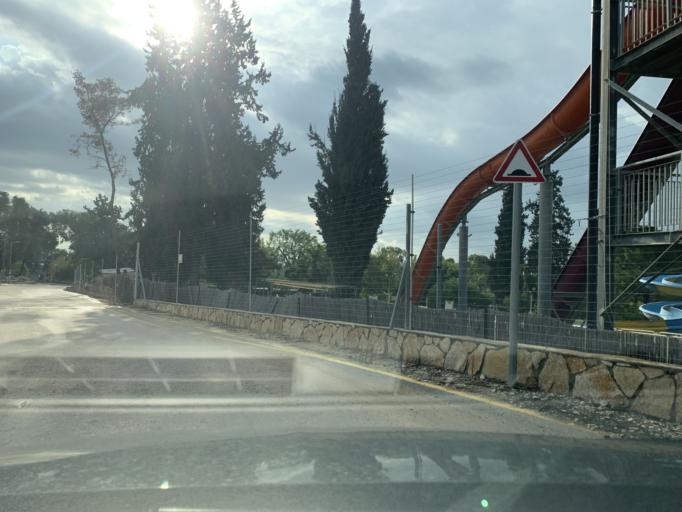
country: IL
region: Central District
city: Rosh Ha'Ayin
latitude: 32.0640
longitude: 34.9492
